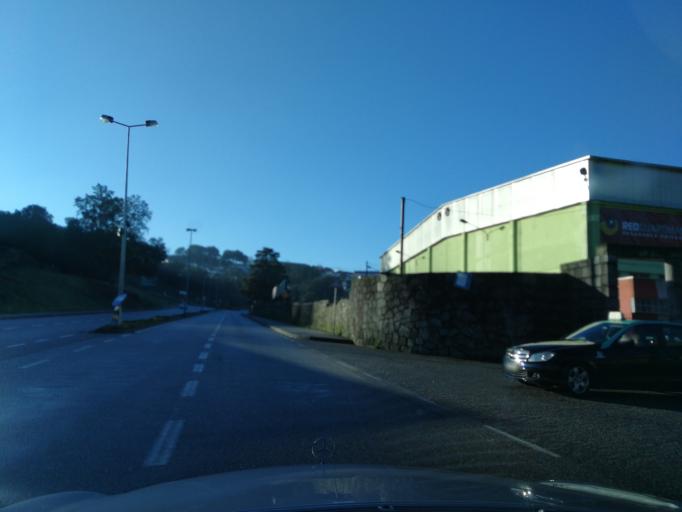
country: PT
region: Braga
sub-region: Braga
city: Braga
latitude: 41.5404
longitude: -8.4191
